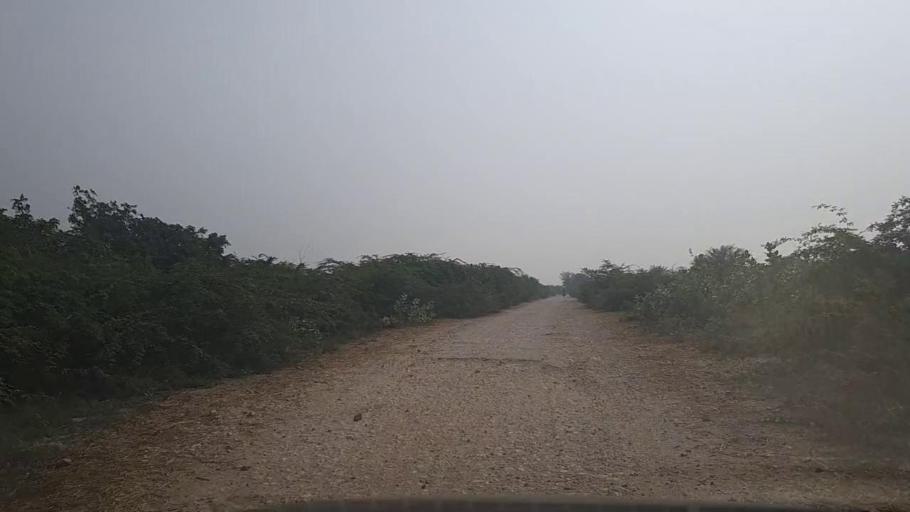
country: PK
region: Sindh
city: Mirpur Sakro
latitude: 24.4837
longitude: 67.6442
